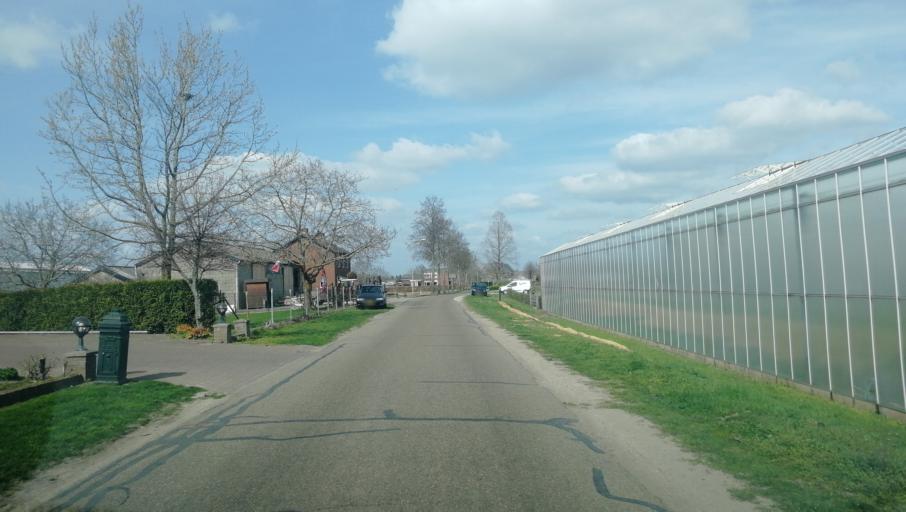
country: NL
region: Limburg
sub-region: Gemeente Beesel
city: Offenbeek
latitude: 51.3192
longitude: 6.0968
